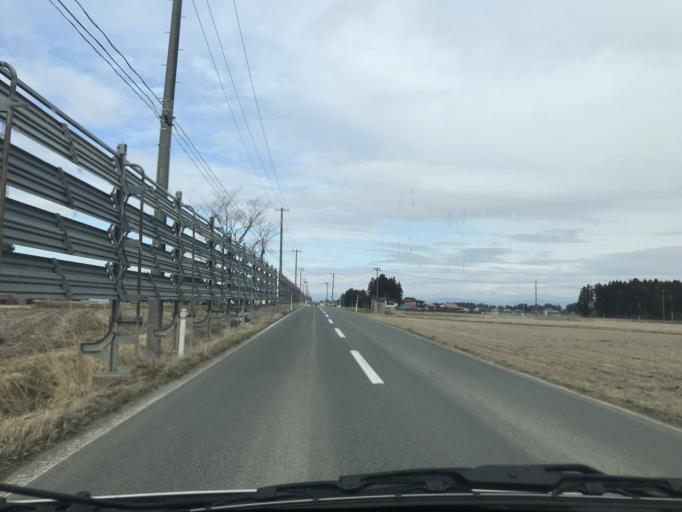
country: JP
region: Iwate
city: Hanamaki
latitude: 39.3406
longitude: 141.0407
